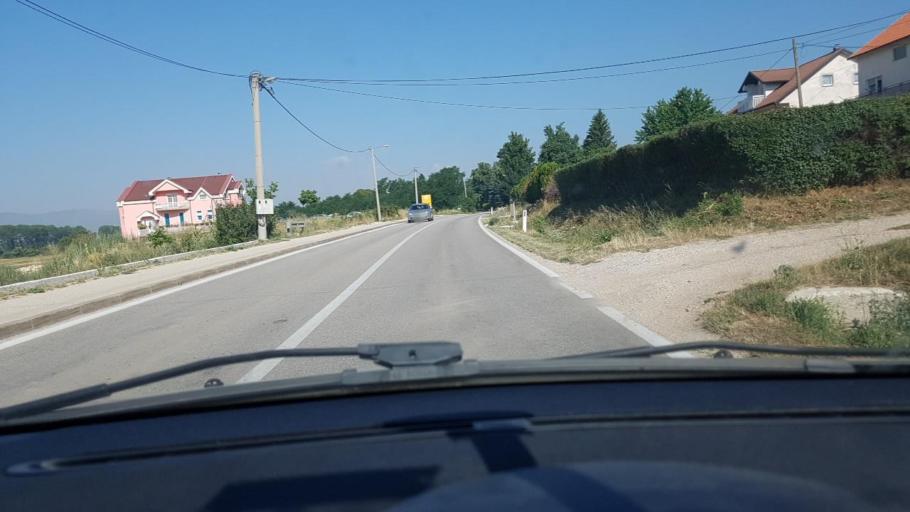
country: BA
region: Federation of Bosnia and Herzegovina
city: Livno
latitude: 43.8315
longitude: 16.9907
